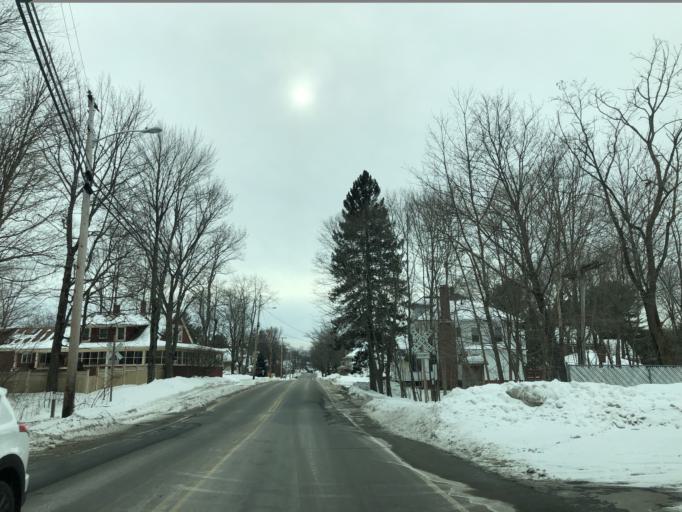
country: US
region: Maine
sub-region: Cumberland County
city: Westbrook
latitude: 43.6864
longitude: -70.3630
